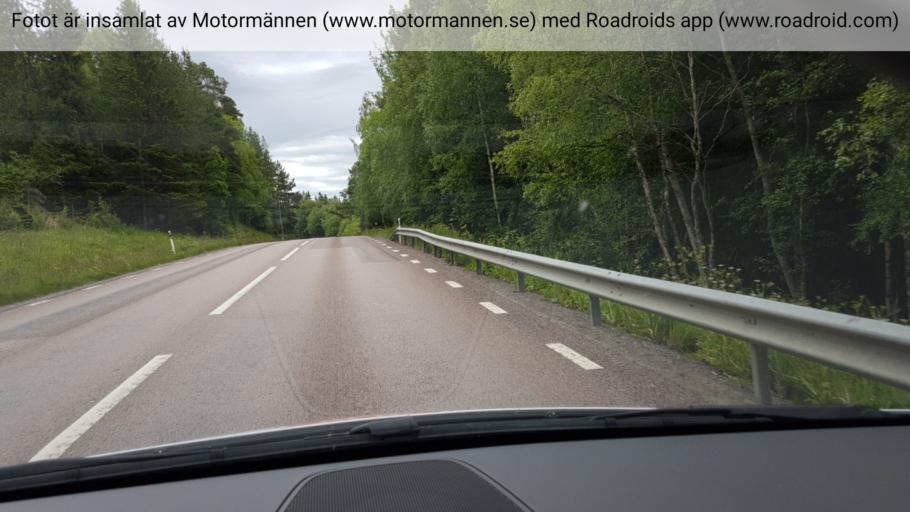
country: SE
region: Jaemtland
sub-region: OEstersunds Kommun
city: Brunflo
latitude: 63.0174
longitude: 14.9503
